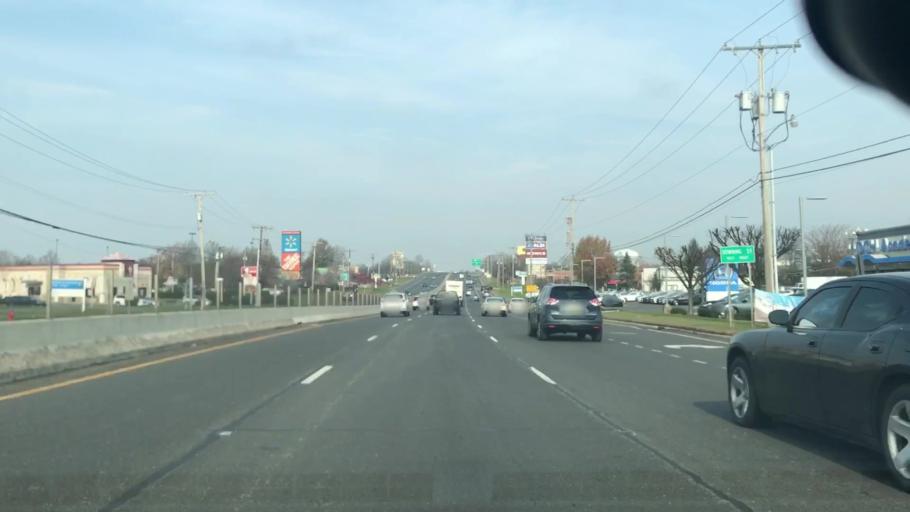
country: US
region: New Jersey
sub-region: Middlesex County
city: Madison Park
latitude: 40.4482
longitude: -74.2992
